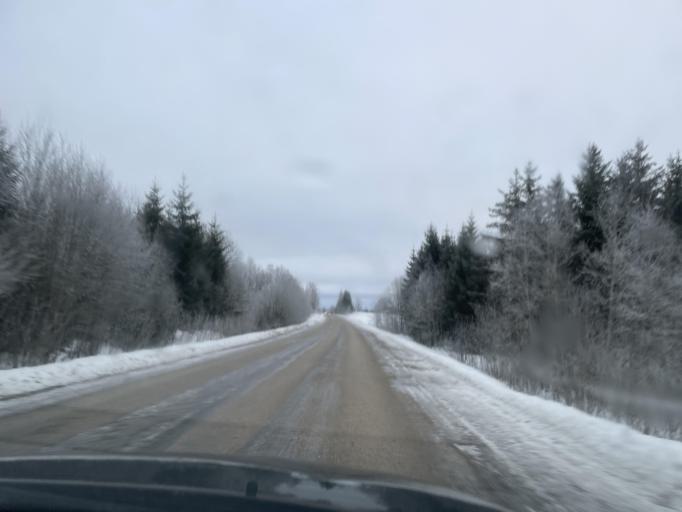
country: LV
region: Rezekne
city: Rezekne
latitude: 56.4985
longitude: 27.3922
